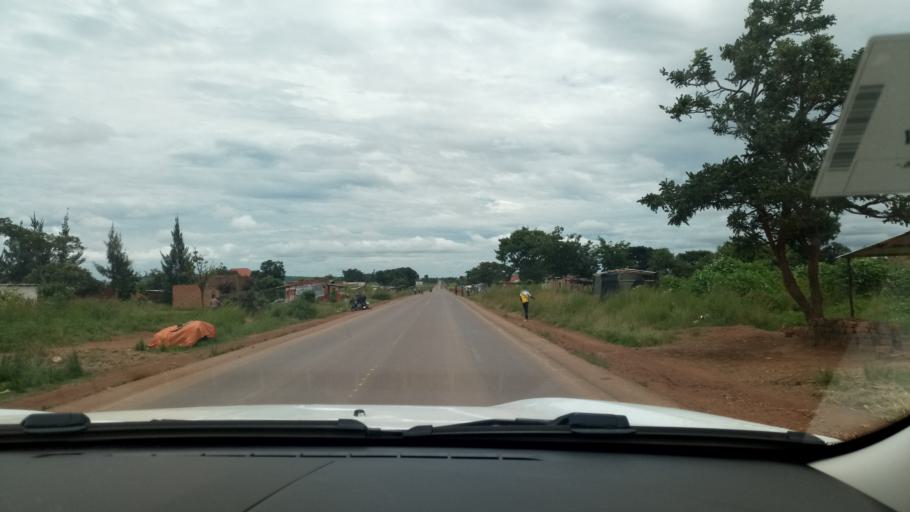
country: CD
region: Katanga
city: Lubumbashi
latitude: -11.5697
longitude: 27.5483
